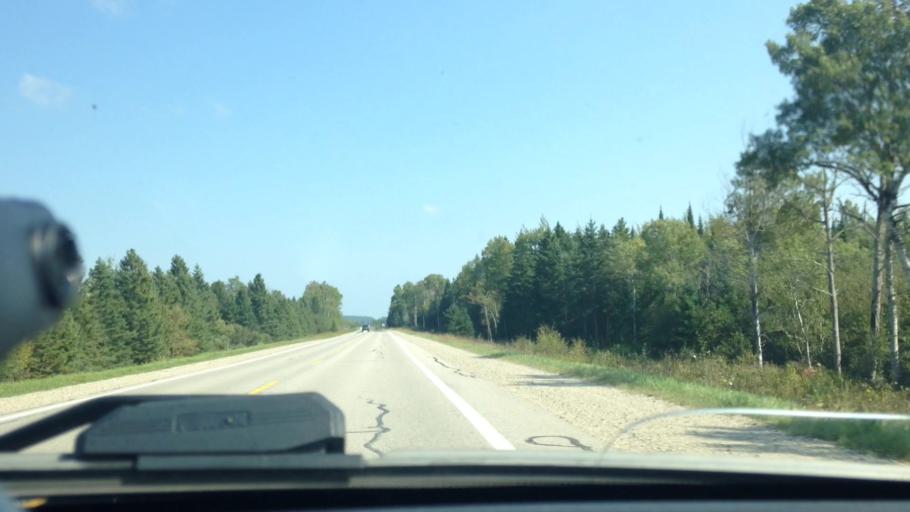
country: US
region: Michigan
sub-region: Luce County
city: Newberry
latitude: 46.3102
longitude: -85.6196
